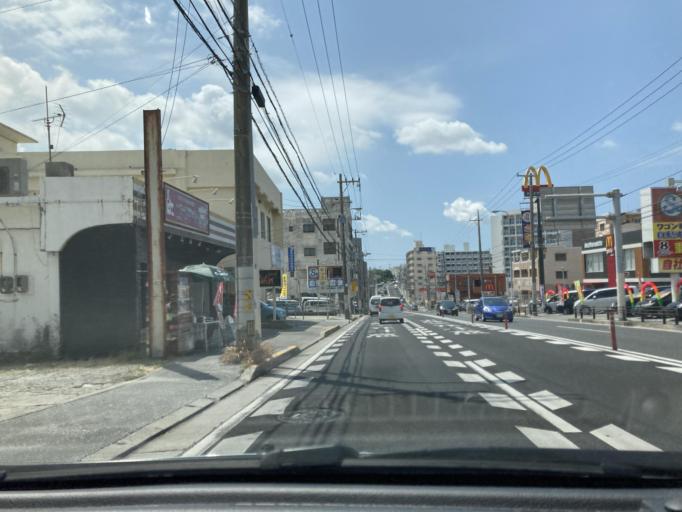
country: JP
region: Okinawa
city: Ginowan
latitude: 26.2609
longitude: 127.7599
